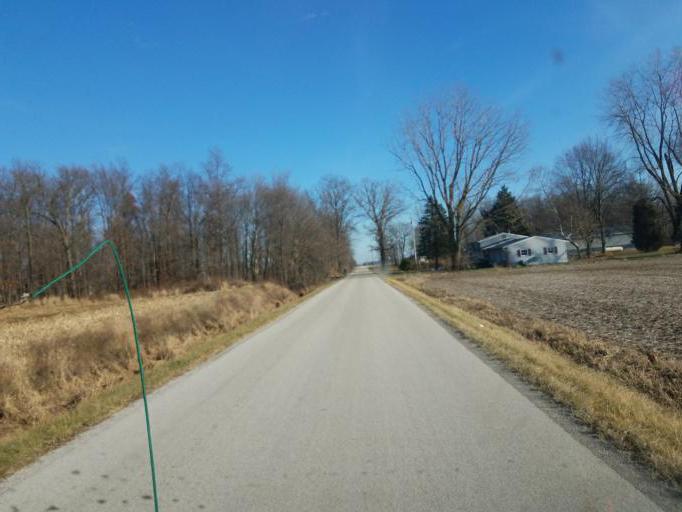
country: US
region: Ohio
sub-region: Morrow County
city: Cardington
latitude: 40.6016
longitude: -82.9291
